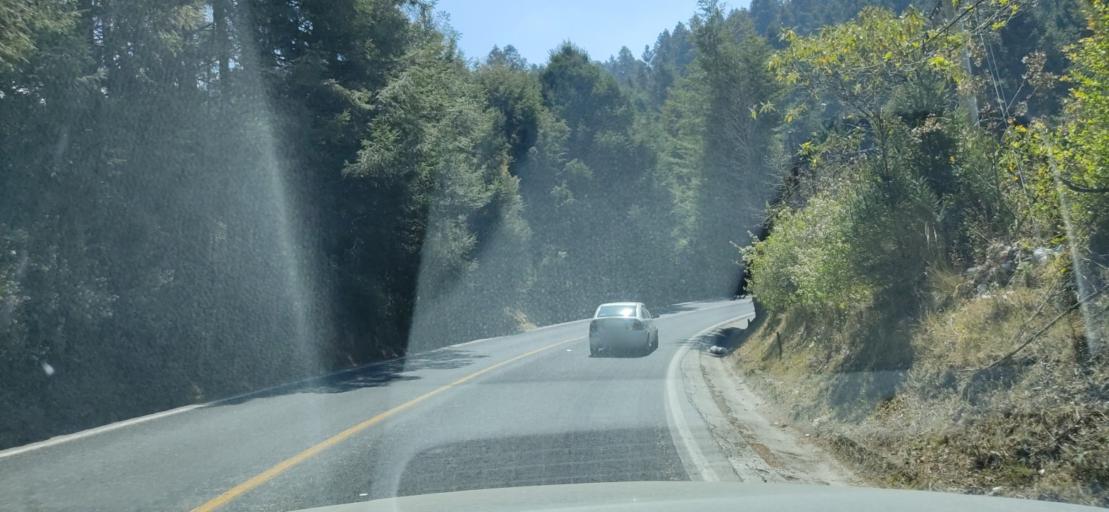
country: MX
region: Mexico
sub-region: Ocoyoacac
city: San Jeronimo Acazulco
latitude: 19.2624
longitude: -99.3716
